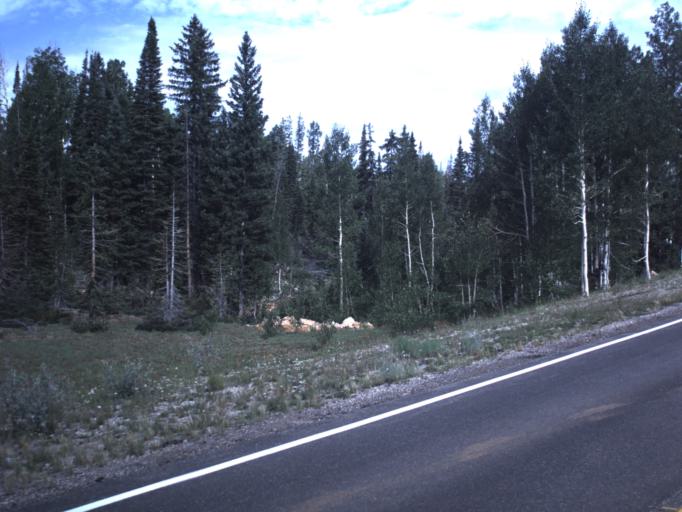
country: US
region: Utah
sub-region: Iron County
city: Parowan
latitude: 37.5494
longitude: -112.7862
